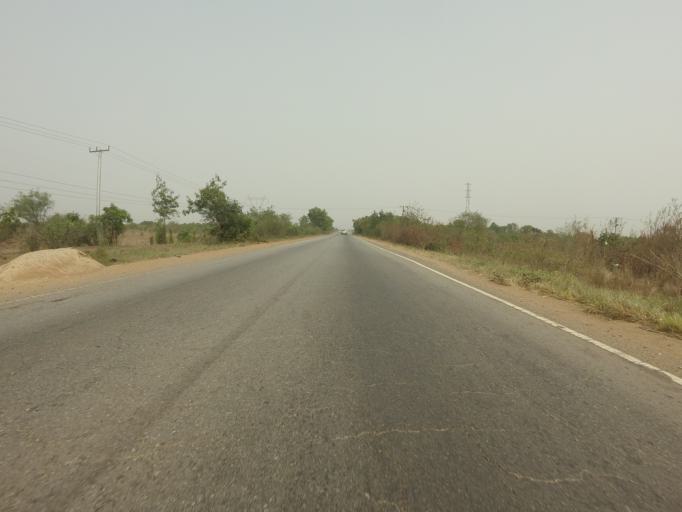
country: GH
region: Greater Accra
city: Tema
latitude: 5.8109
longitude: 0.1624
